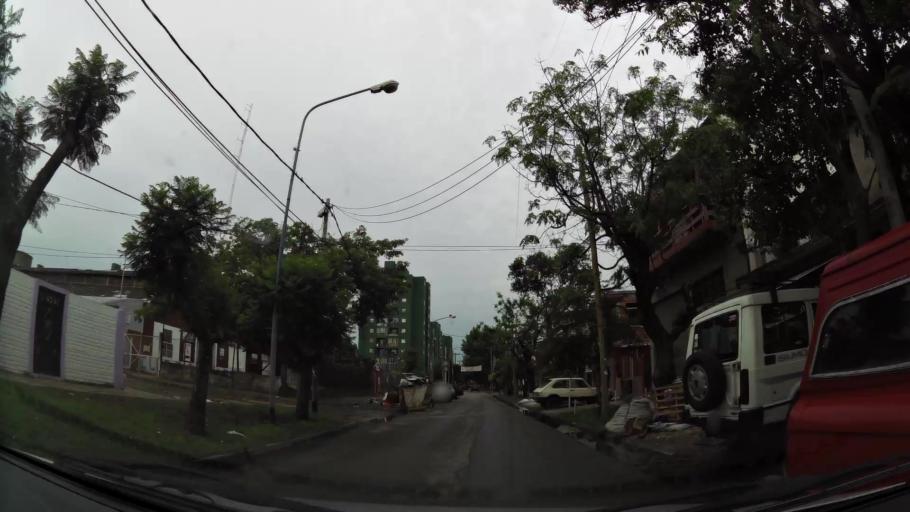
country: AR
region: Buenos Aires
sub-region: Partido de Lanus
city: Lanus
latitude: -34.7115
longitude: -58.3559
